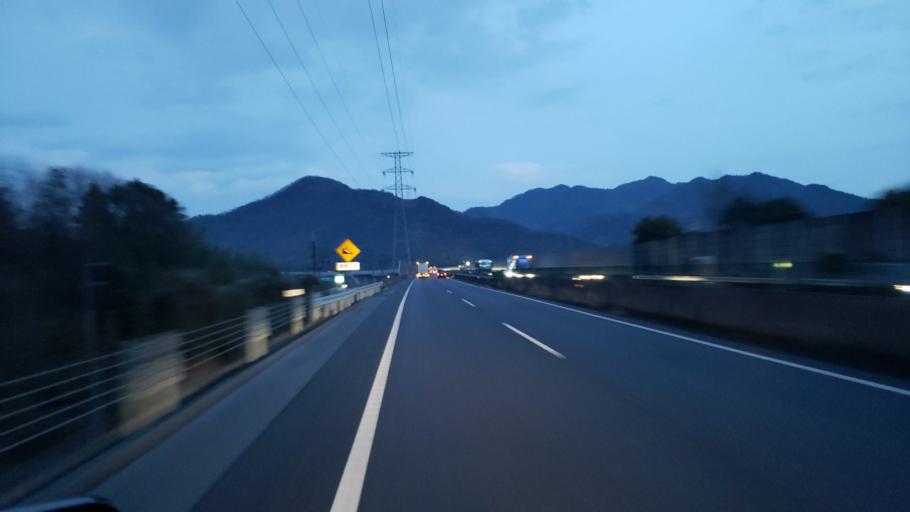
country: JP
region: Hyogo
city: Himeji
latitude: 34.8502
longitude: 134.7481
